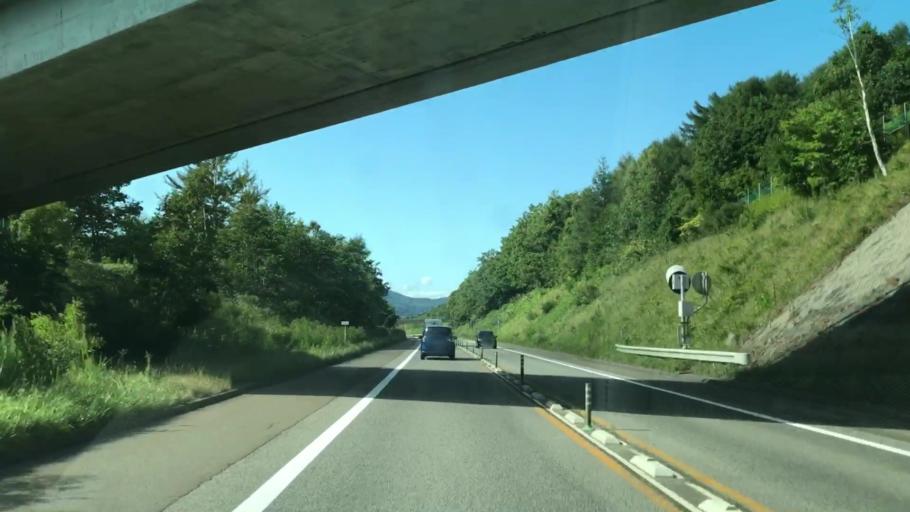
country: JP
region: Hokkaido
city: Date
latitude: 42.4731
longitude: 140.9044
